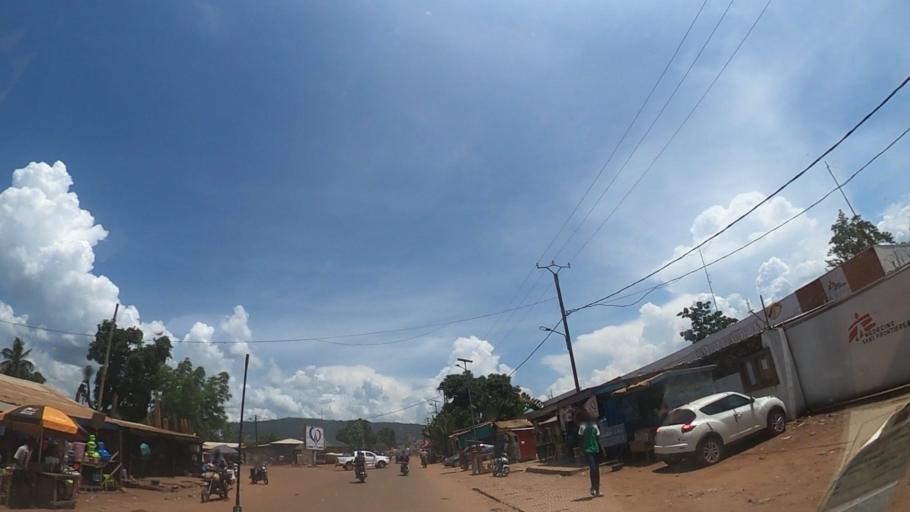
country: CF
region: Bangui
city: Bangui
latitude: 4.3604
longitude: 18.5604
